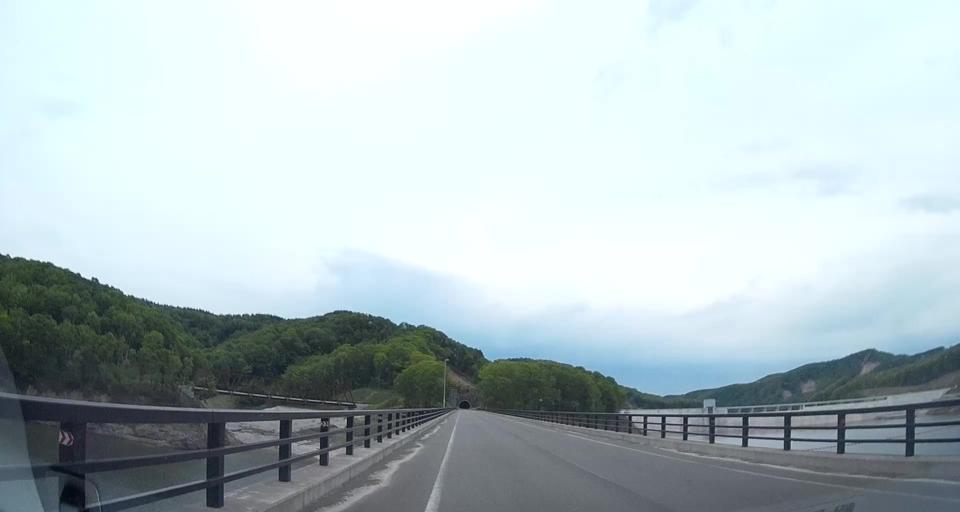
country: JP
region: Hokkaido
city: Chitose
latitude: 42.7670
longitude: 142.0007
